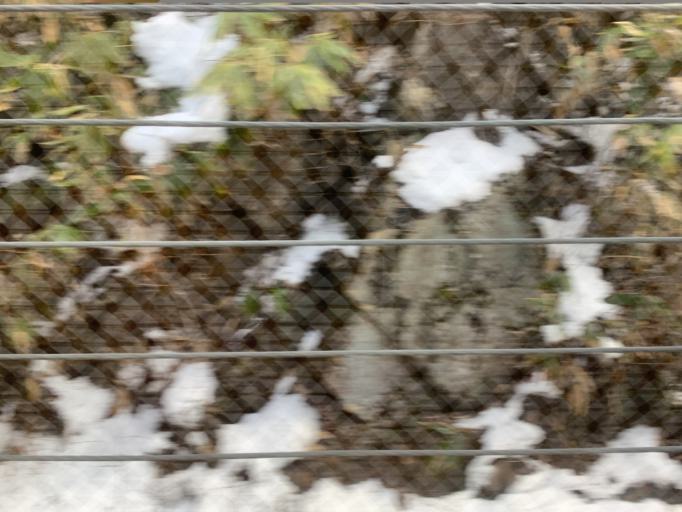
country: JP
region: Gifu
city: Takayama
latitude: 36.0451
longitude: 137.2787
